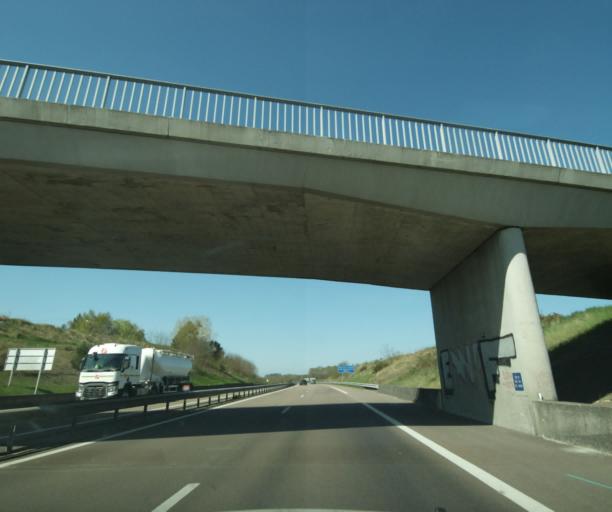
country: FR
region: Bourgogne
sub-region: Departement de la Nievre
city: Cosne-Cours-sur-Loire
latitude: 47.4158
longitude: 2.9463
